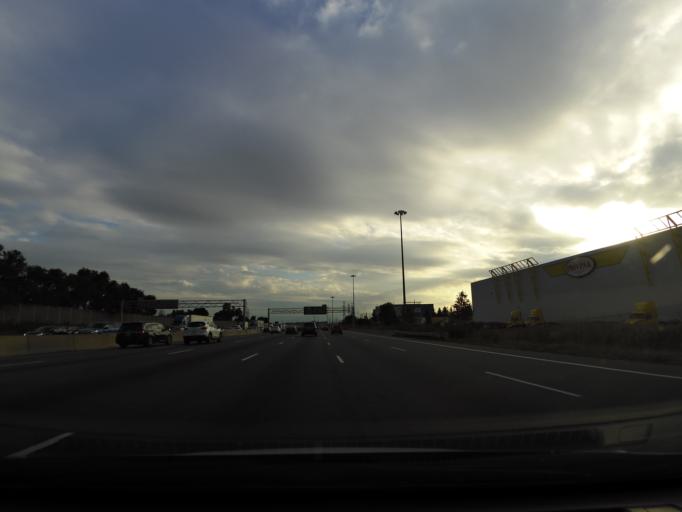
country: CA
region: Ontario
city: Etobicoke
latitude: 43.6866
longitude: -79.5727
